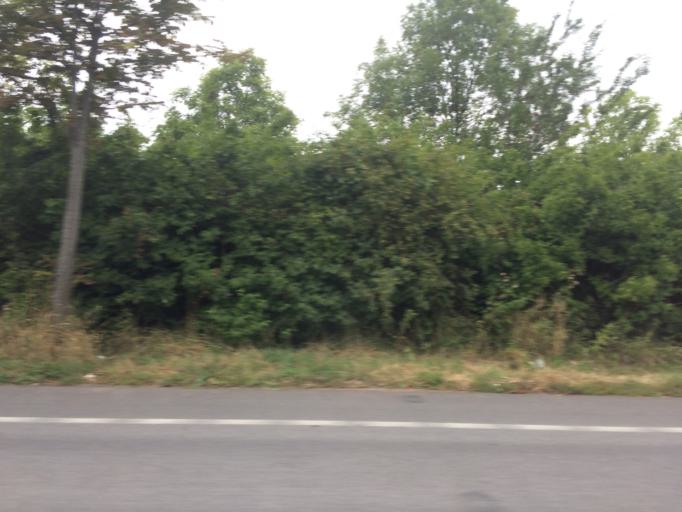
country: DE
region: Saxony
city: Wilsdruff
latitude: 51.0592
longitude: 13.5393
